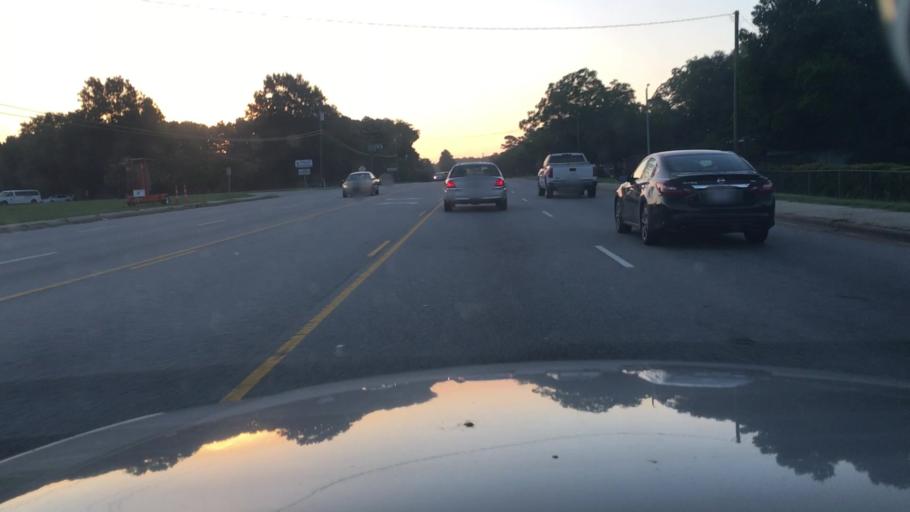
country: US
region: North Carolina
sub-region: Cumberland County
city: Fort Bragg
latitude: 35.0583
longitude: -78.9914
